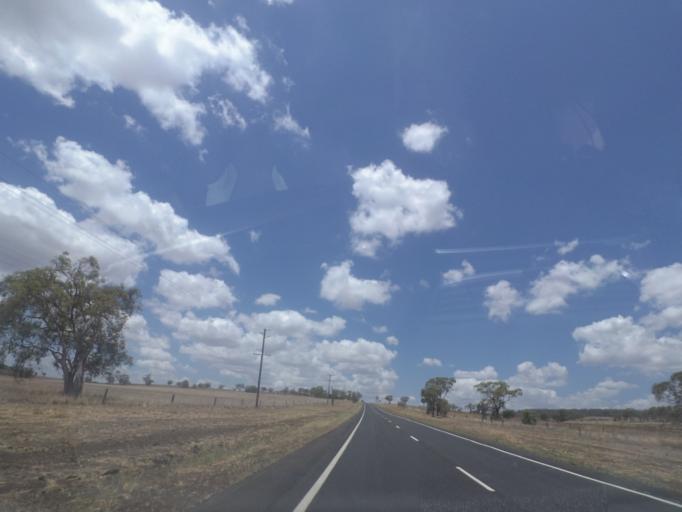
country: AU
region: Queensland
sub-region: Toowoomba
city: Top Camp
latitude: -27.7247
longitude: 151.9117
